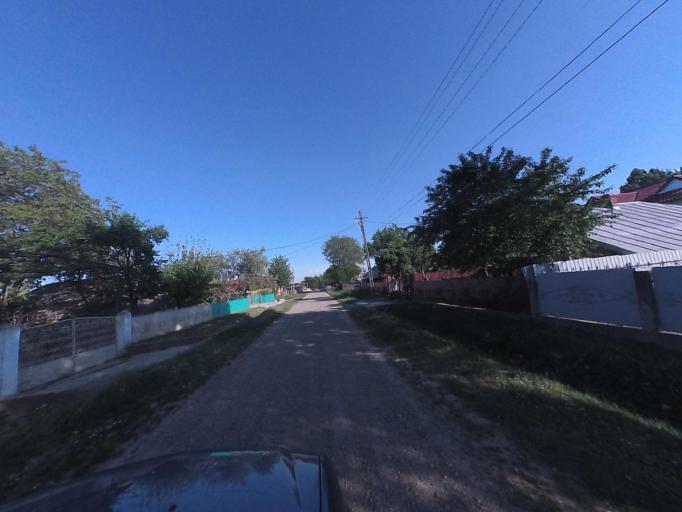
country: RO
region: Neamt
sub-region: Comuna Cordun
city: Pildesti
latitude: 46.9845
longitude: 26.8062
